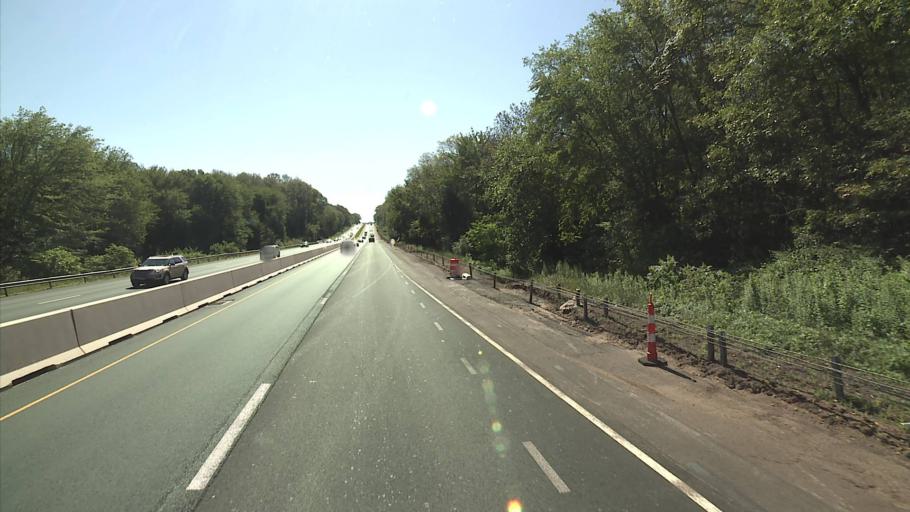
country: US
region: Connecticut
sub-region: Middlesex County
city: Old Saybrook Center
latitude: 41.3226
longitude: -72.3222
